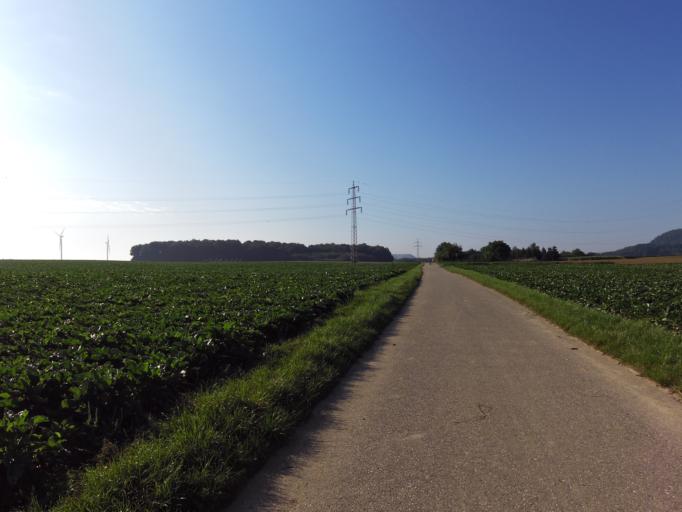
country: DE
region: North Rhine-Westphalia
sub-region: Regierungsbezirk Koln
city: Ubach-Palenberg
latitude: 50.9083
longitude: 6.1221
